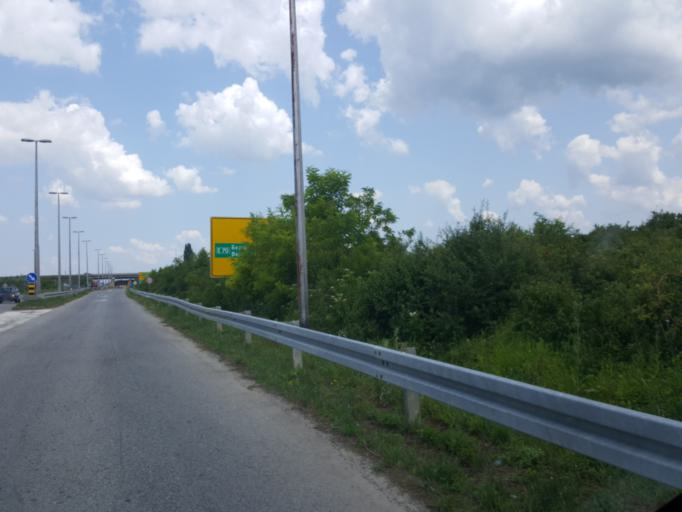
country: RS
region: Autonomna Pokrajina Vojvodina
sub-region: Sremski Okrug
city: Sid
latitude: 45.0442
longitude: 19.2136
